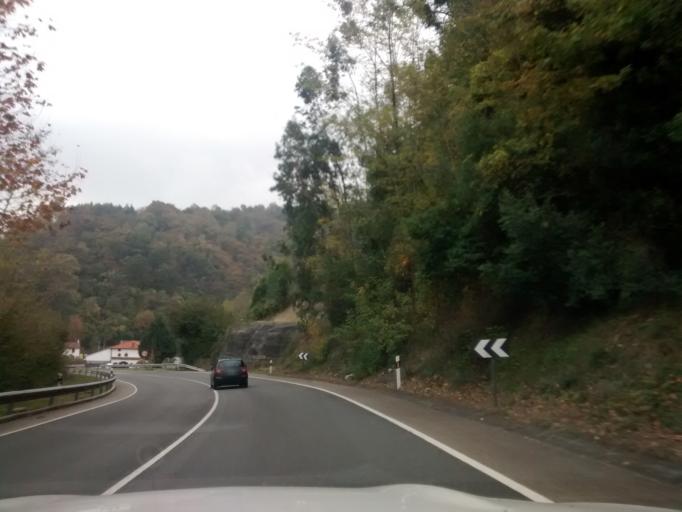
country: ES
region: Cantabria
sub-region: Provincia de Cantabria
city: Santiurde de Toranzo
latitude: 43.2384
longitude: -3.9486
